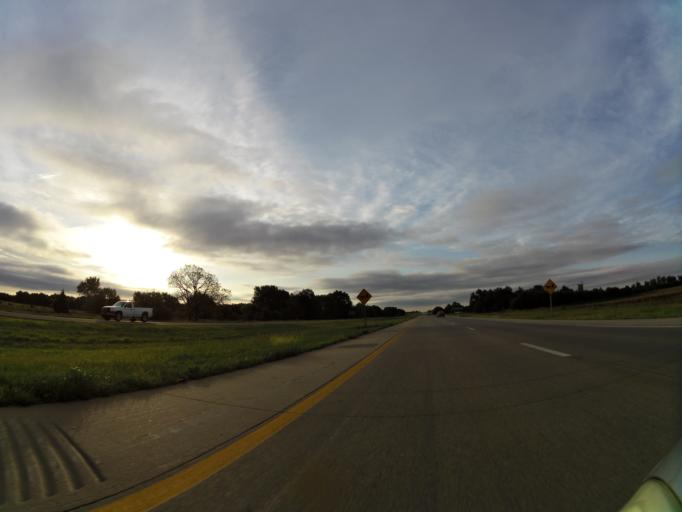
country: US
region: Kansas
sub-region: Reno County
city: Haven
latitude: 37.9304
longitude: -97.8515
